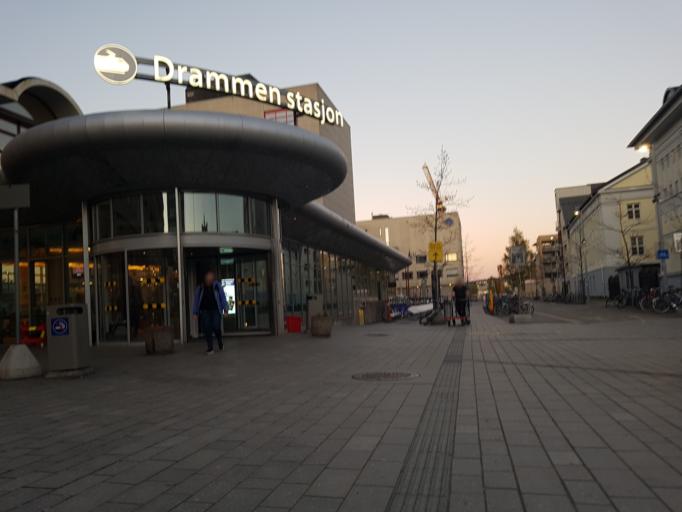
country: NO
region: Buskerud
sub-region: Drammen
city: Drammen
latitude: 59.7402
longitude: 10.2030
